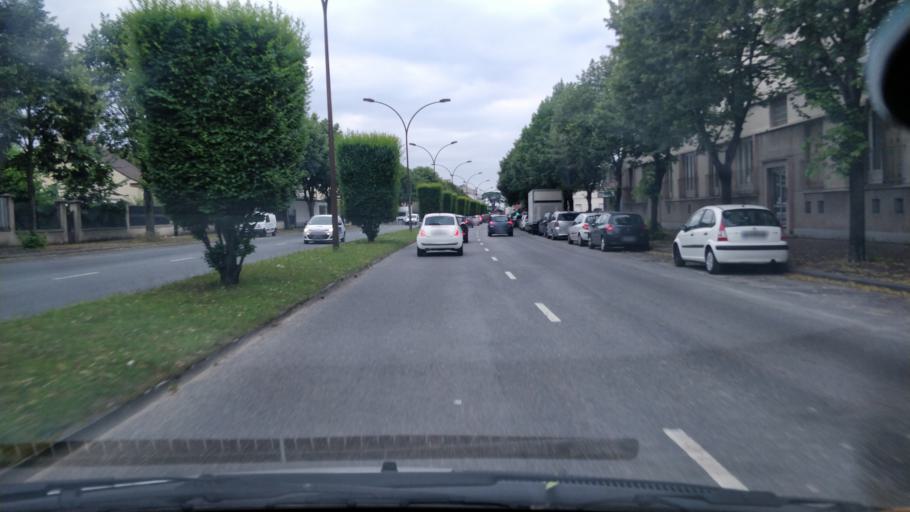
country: FR
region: Ile-de-France
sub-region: Departement de Seine-Saint-Denis
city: Livry-Gargan
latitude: 48.9244
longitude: 2.5473
